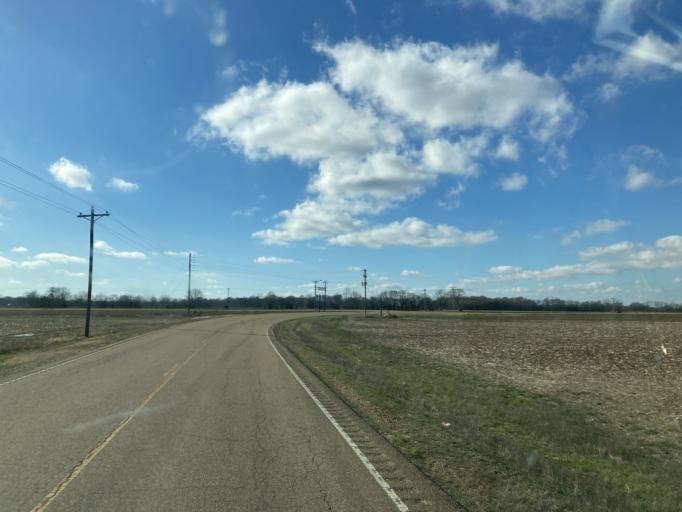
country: US
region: Mississippi
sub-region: Yazoo County
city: Yazoo City
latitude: 32.9619
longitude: -90.4913
